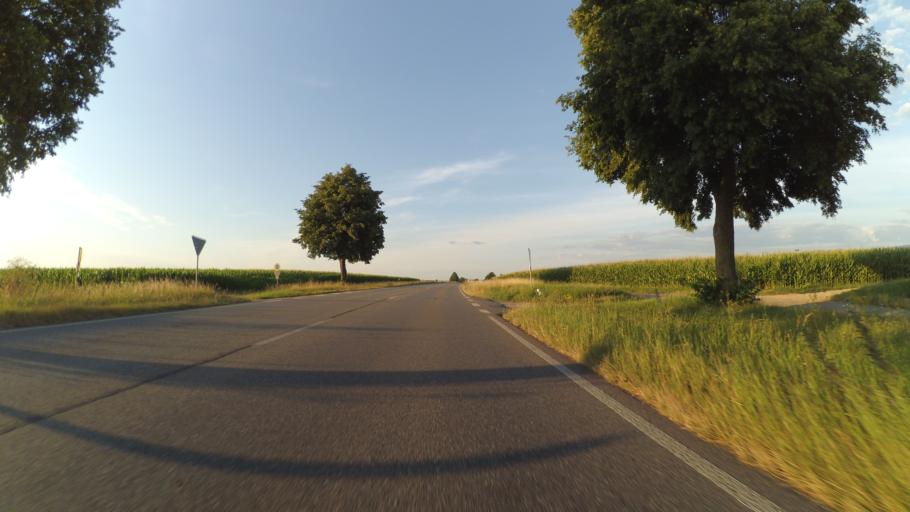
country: DE
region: Baden-Wuerttemberg
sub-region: Freiburg Region
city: Eschbach
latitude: 47.8945
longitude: 7.6731
